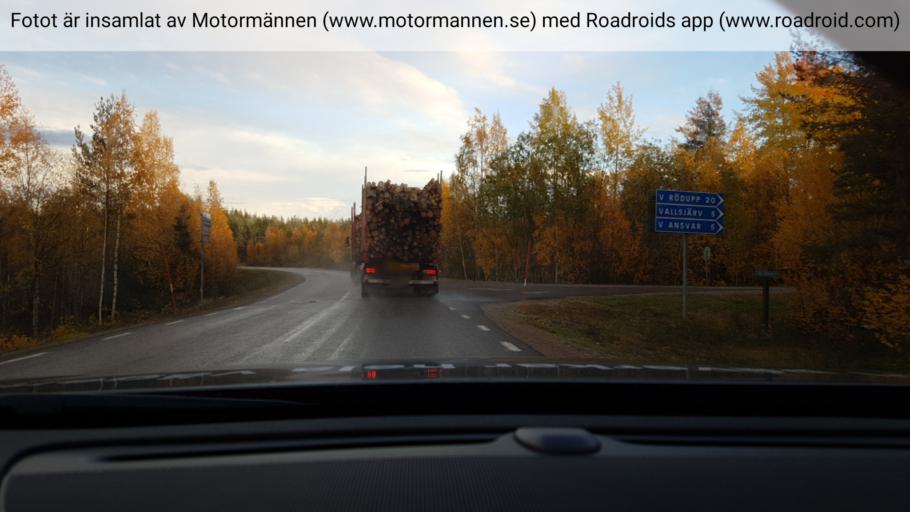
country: SE
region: Norrbotten
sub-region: Overkalix Kommun
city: OEverkalix
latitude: 66.6490
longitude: 22.6995
